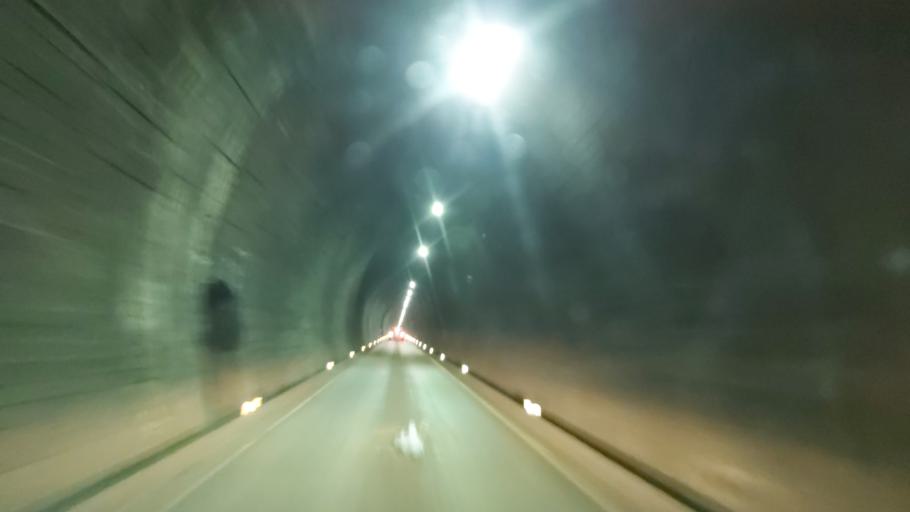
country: CL
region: Araucania
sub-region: Provincia de Cautin
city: Vilcun
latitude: -38.5333
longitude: -71.5095
